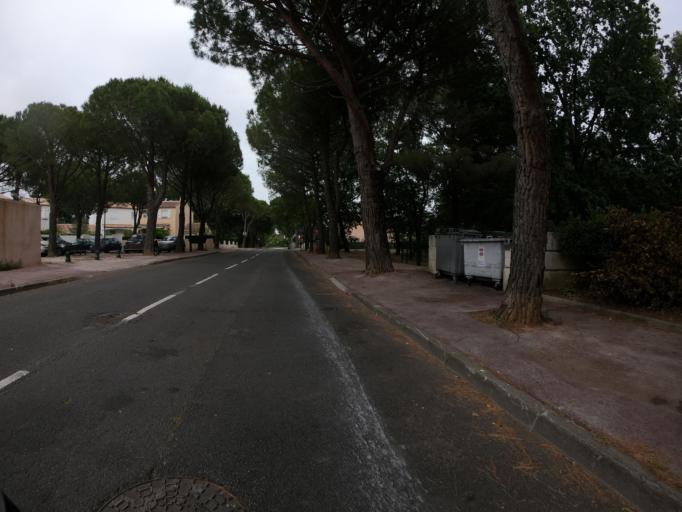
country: FR
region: Provence-Alpes-Cote d'Azur
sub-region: Departement du Var
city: La Garde
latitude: 43.1309
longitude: 6.0210
